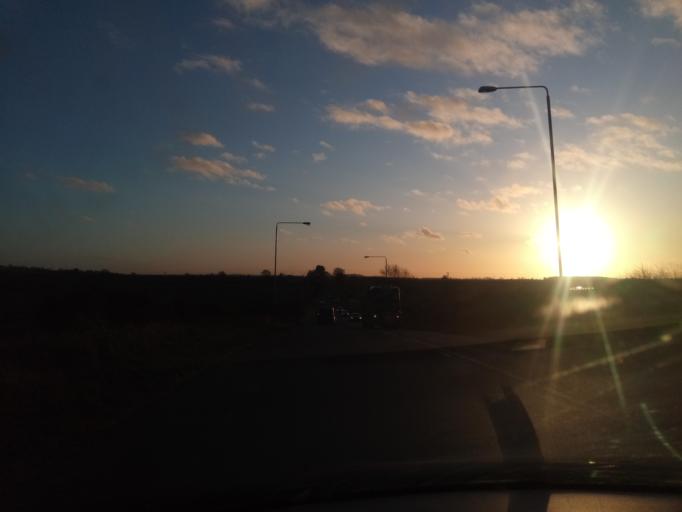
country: GB
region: England
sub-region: Nottinghamshire
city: Farnsfield
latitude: 53.0966
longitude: -1.0668
